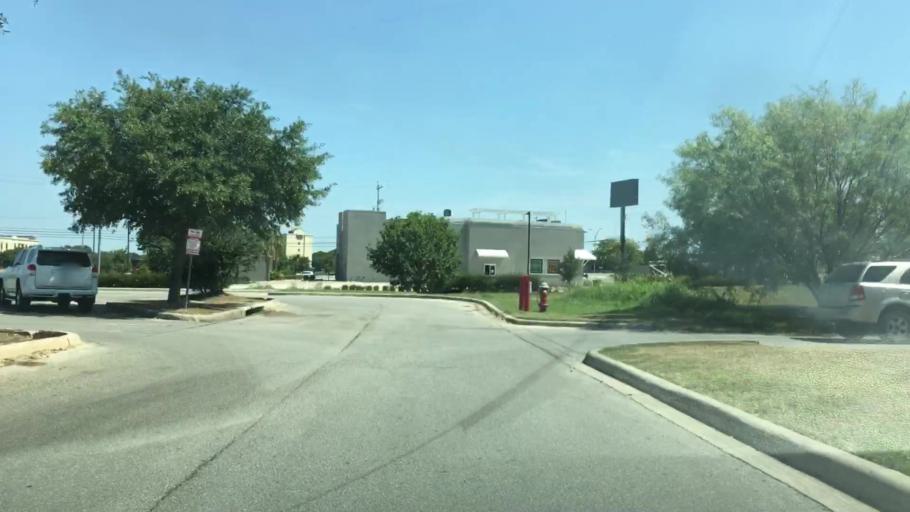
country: US
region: Texas
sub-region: Bexar County
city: Selma
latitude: 29.6024
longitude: -98.2766
